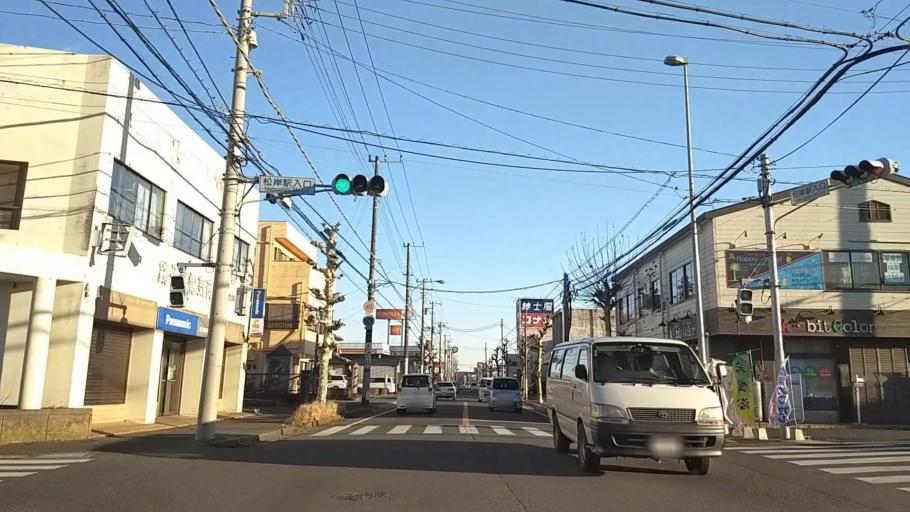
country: JP
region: Chiba
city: Hasaki
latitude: 35.7416
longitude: 140.7949
